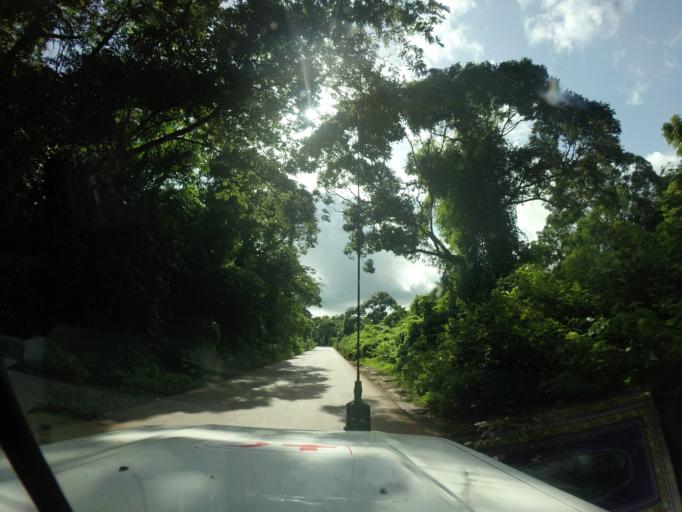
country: GN
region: Mamou
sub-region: Mamou Prefecture
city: Mamou
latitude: 10.3504
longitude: -12.1811
